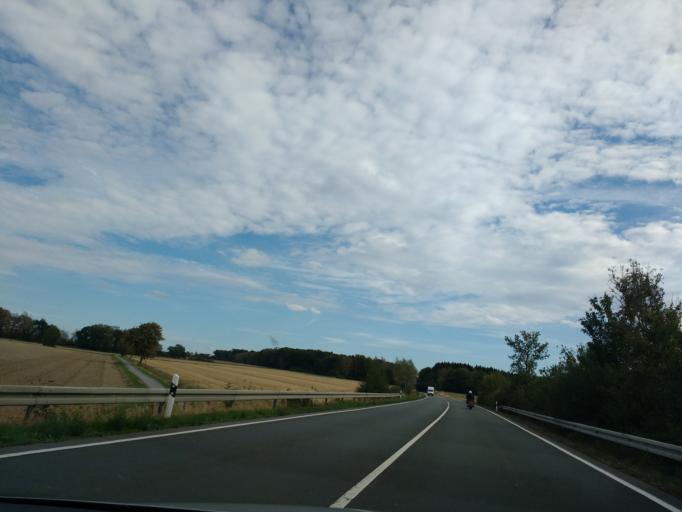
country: DE
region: North Rhine-Westphalia
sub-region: Regierungsbezirk Arnsberg
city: Anrochte
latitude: 51.5425
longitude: 8.3115
